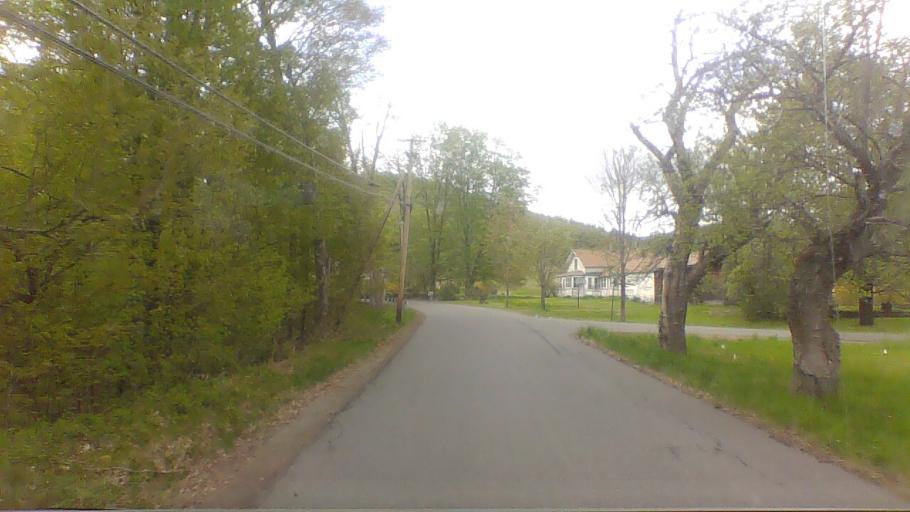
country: US
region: Massachusetts
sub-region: Franklin County
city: Buckland
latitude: 42.5805
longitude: -72.8156
